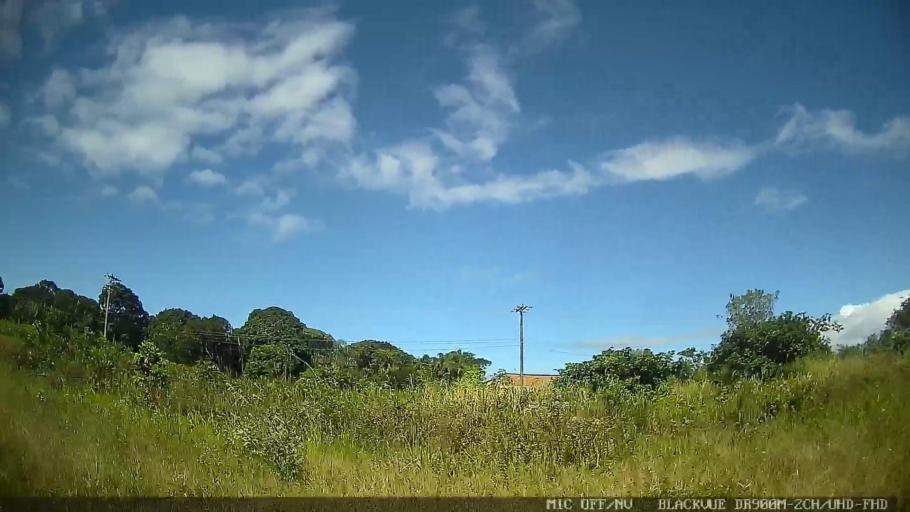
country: BR
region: Sao Paulo
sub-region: Itanhaem
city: Itanhaem
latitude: -24.2298
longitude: -46.8822
